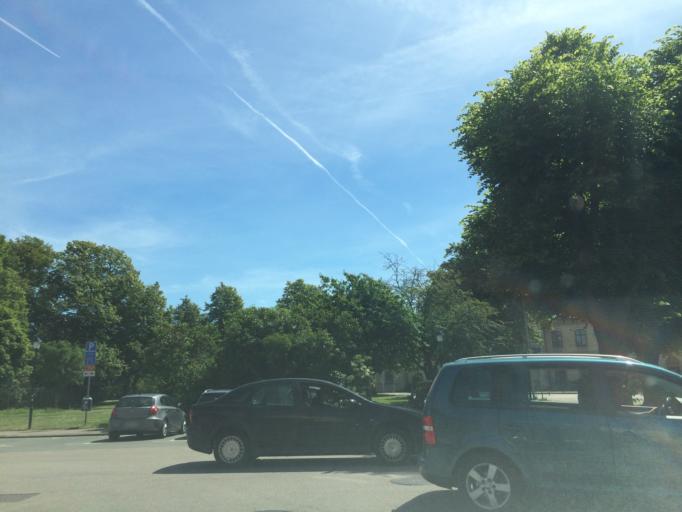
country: SE
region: Skane
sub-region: Landskrona
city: Landskrona
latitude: 55.8681
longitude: 12.8302
